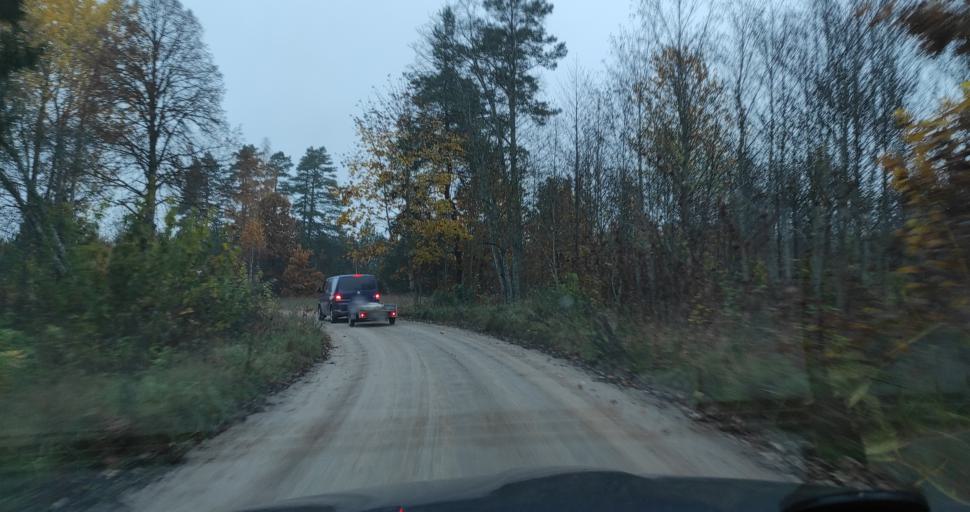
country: LV
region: Pavilostas
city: Pavilosta
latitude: 56.7620
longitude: 21.2741
